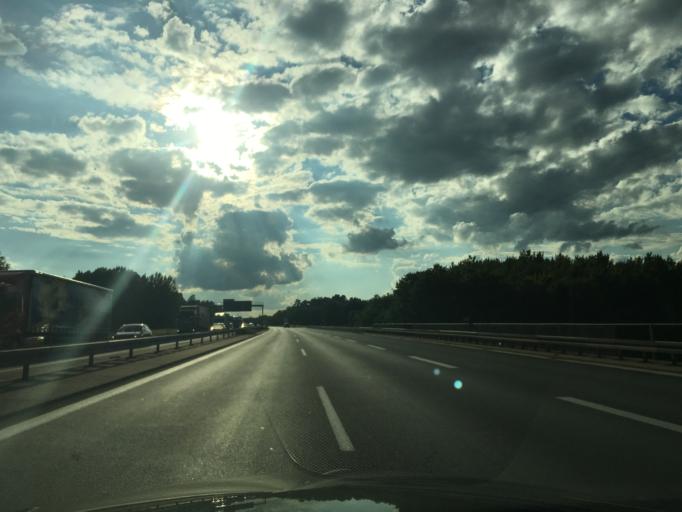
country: DE
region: Bavaria
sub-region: Regierungsbezirk Mittelfranken
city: Burgoberbach
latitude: 49.2570
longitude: 10.5900
